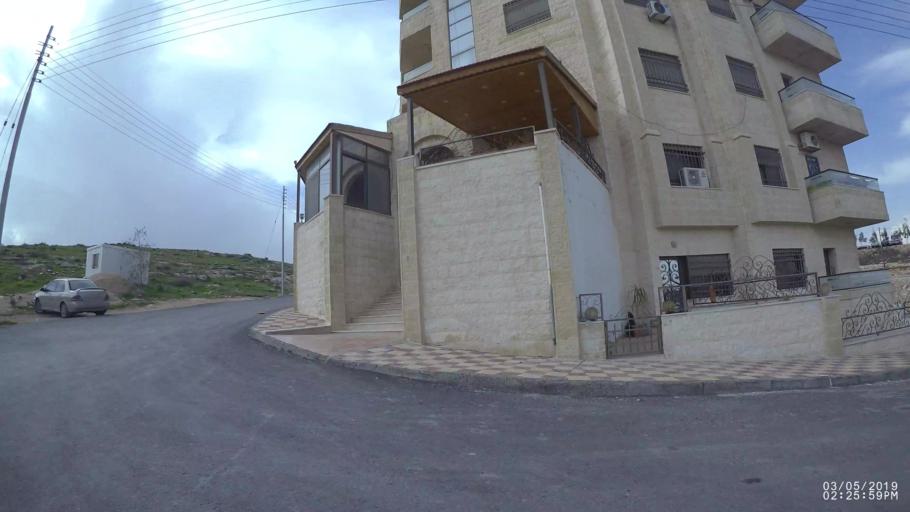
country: JO
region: Amman
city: Amman
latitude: 32.0155
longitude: 35.9430
